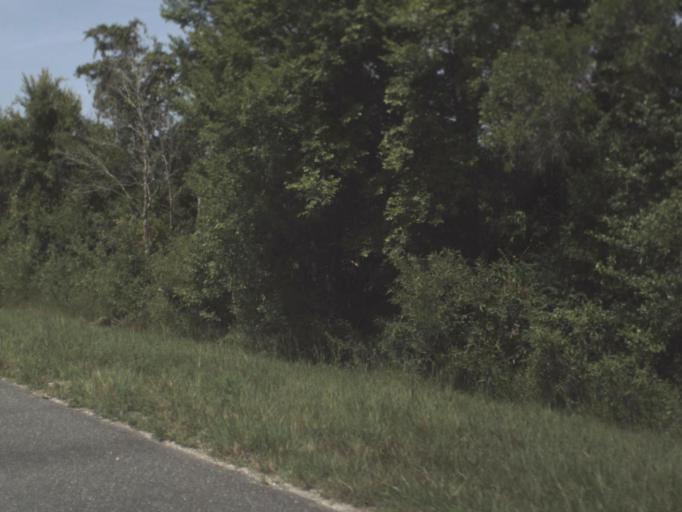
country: US
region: Florida
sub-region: Taylor County
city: Steinhatchee
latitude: 29.7449
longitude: -83.3549
